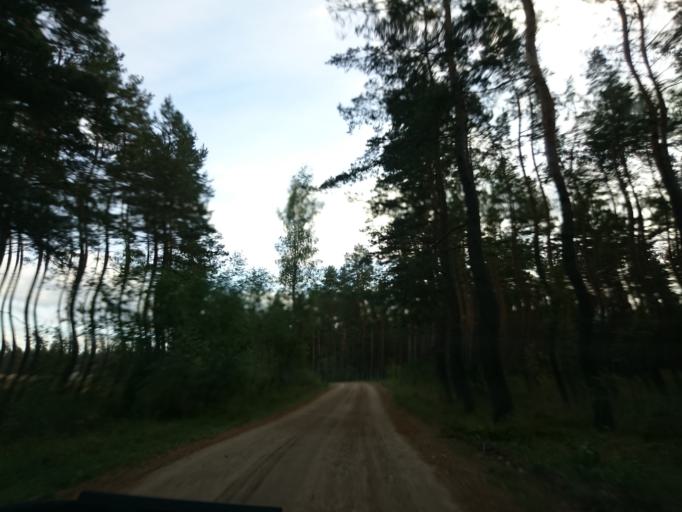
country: LV
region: Garkalne
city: Garkalne
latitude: 57.0416
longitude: 24.3875
